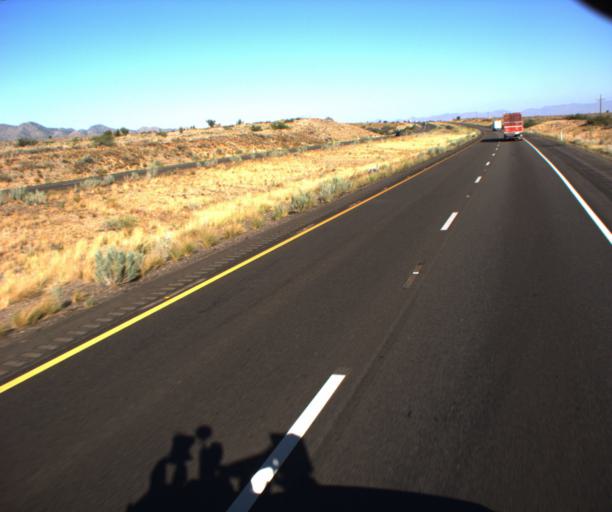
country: US
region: Arizona
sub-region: Mohave County
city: New Kingman-Butler
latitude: 35.1911
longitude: -113.8219
